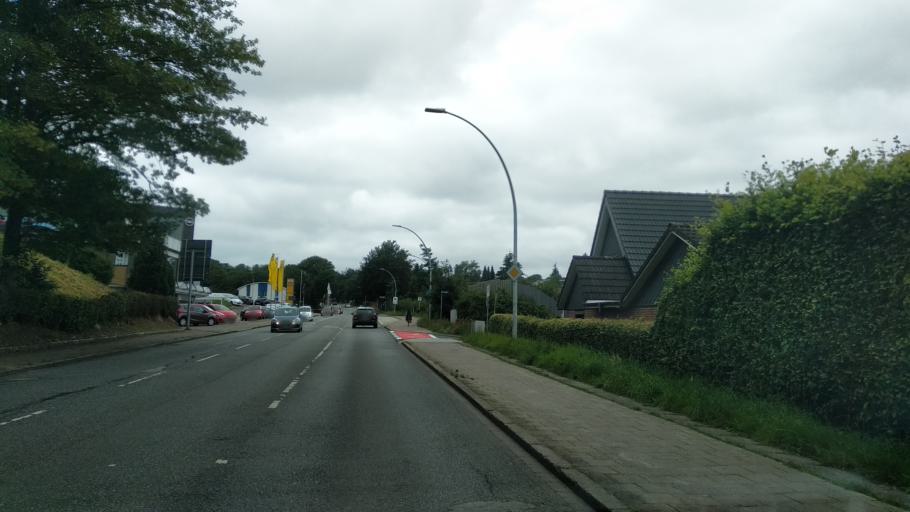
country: DE
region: Schleswig-Holstein
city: Schleswig
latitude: 54.5245
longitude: 9.5418
